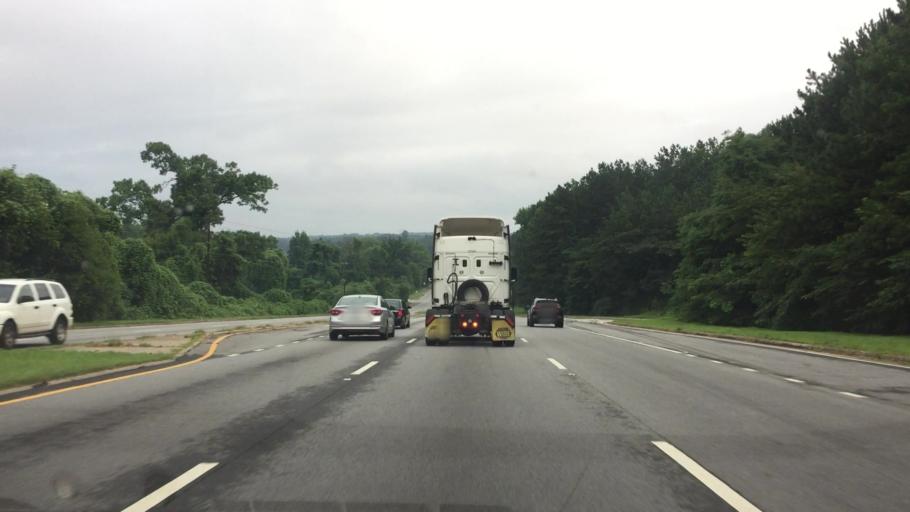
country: US
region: Georgia
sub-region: Clayton County
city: Conley
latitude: 33.6761
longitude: -84.3439
